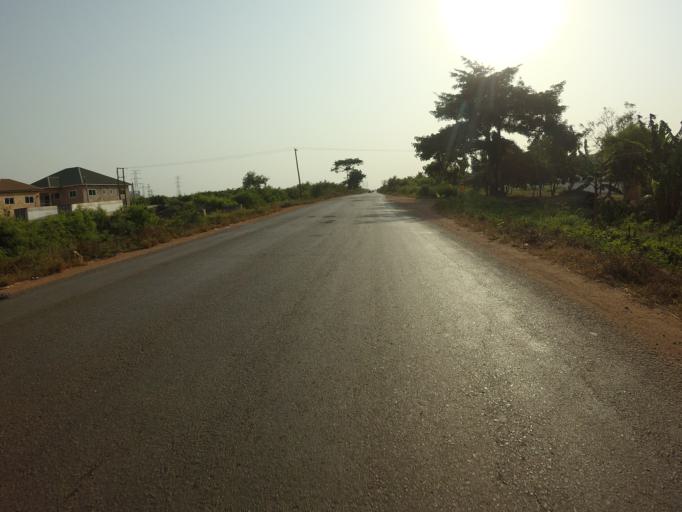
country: GH
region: Greater Accra
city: Tema
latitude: 5.6898
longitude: 0.0470
